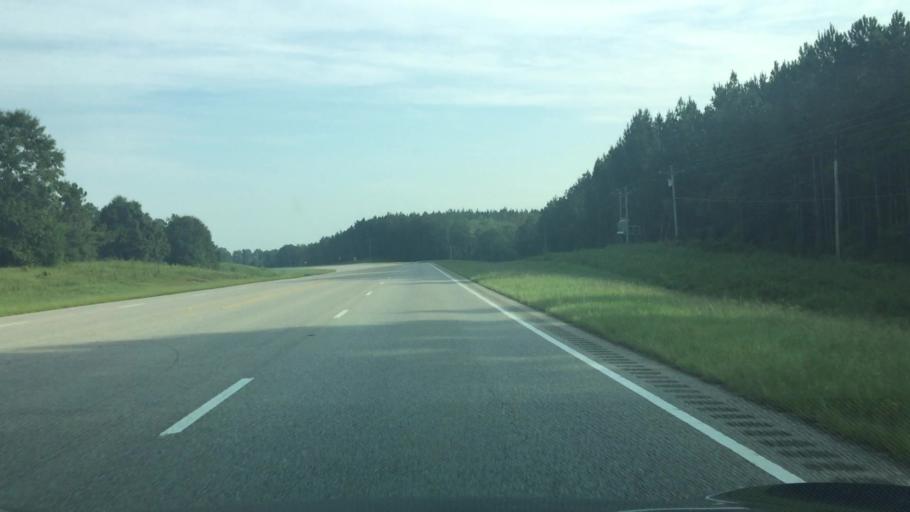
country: US
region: Alabama
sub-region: Covington County
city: Andalusia
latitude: 31.4370
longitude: -86.6117
